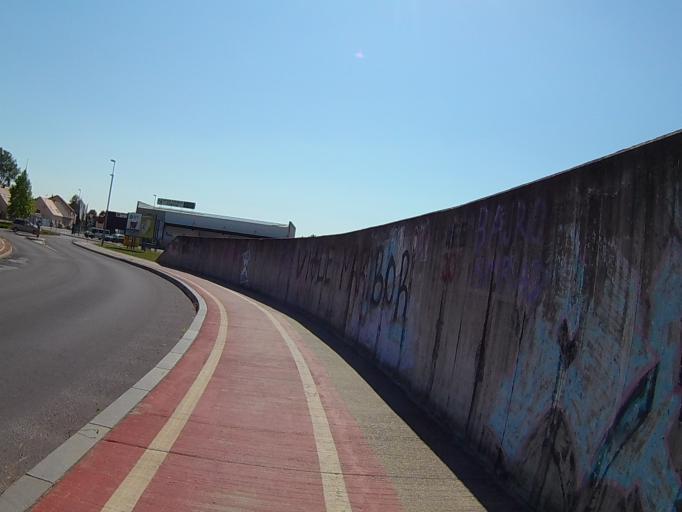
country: SI
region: Maribor
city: Kamnica
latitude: 46.5570
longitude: 15.6248
